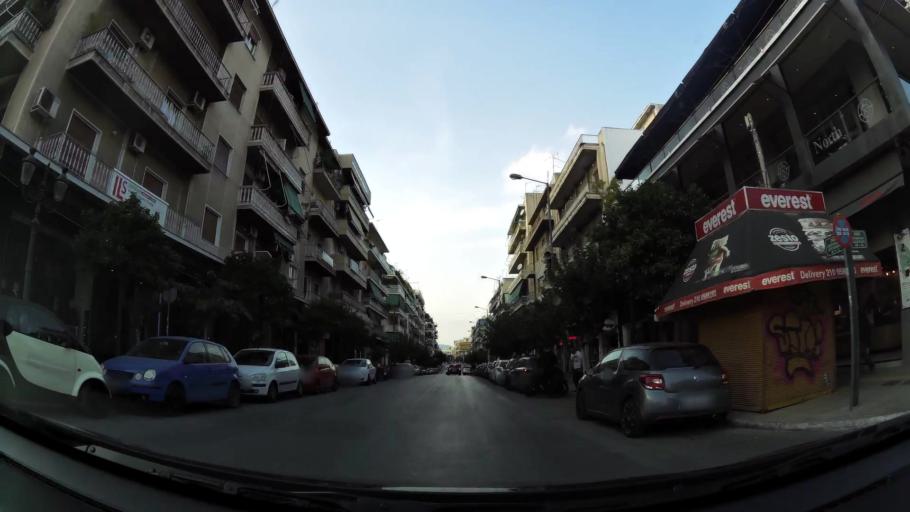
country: GR
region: Attica
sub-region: Nomarchia Athinas
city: Kallithea
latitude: 37.9576
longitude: 23.7003
